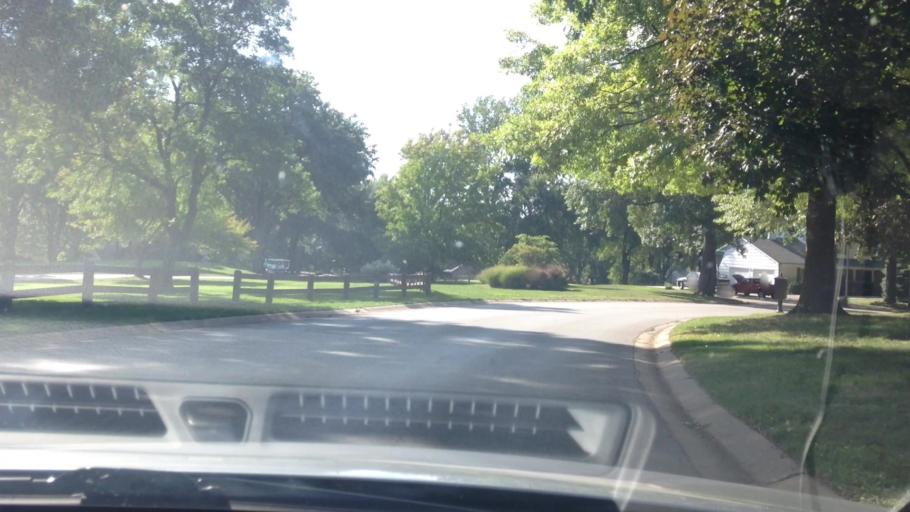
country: US
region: Kansas
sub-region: Johnson County
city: Leawood
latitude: 38.8980
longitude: -94.6210
